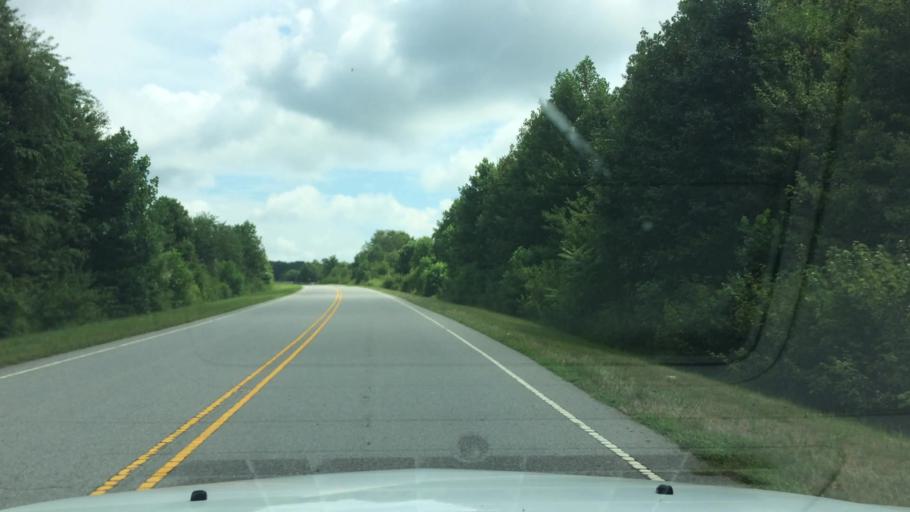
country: US
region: North Carolina
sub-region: Yadkin County
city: Jonesville
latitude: 36.1238
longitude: -80.8472
